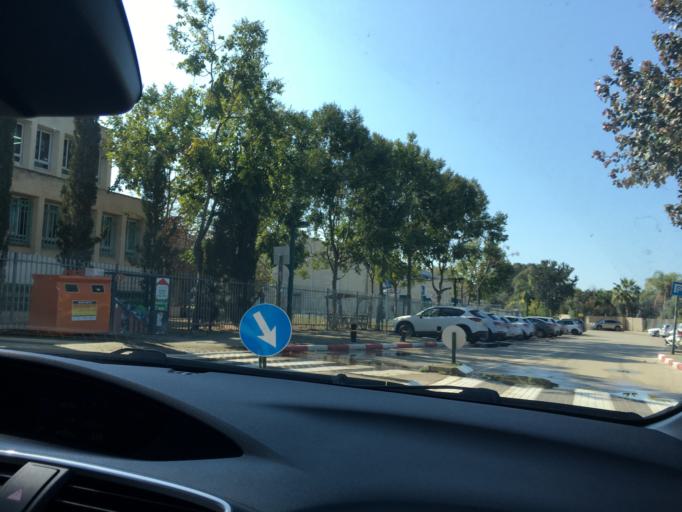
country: IL
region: Tel Aviv
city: Ramat HaSharon
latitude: 32.1504
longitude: 34.8309
